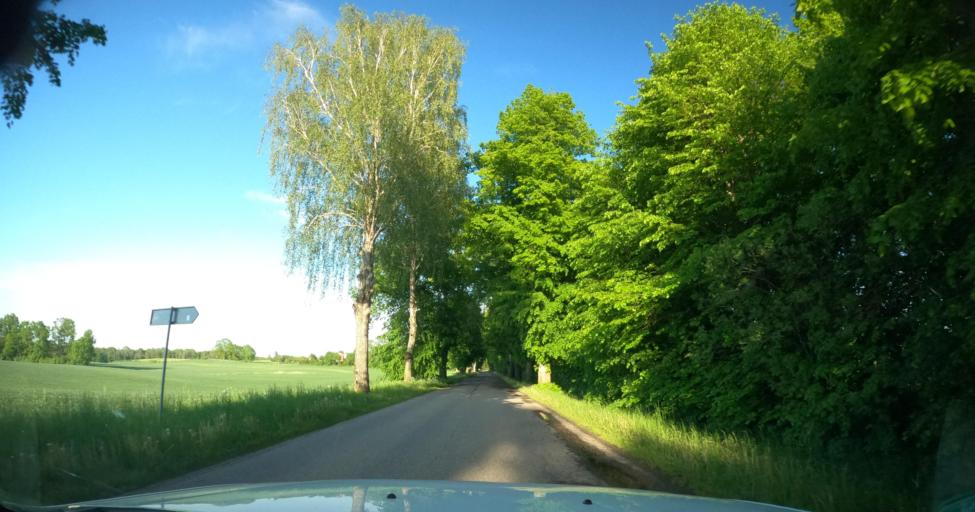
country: PL
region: Warmian-Masurian Voivodeship
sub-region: Powiat braniewski
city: Pieniezno
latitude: 54.2547
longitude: 19.9745
